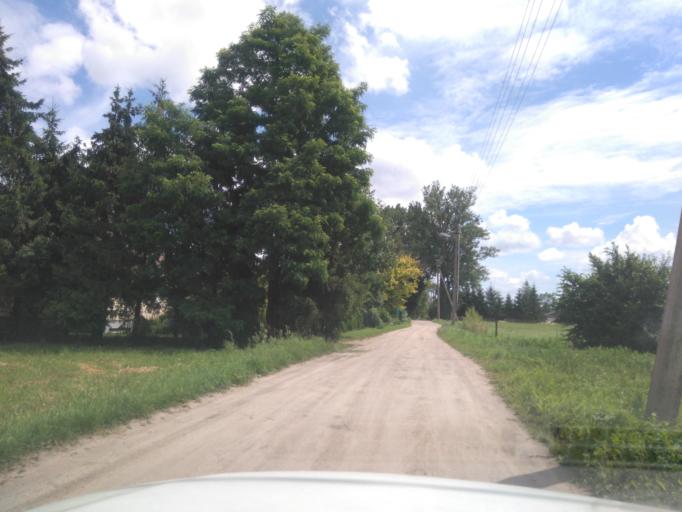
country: LT
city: Virbalis
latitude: 54.6301
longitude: 22.8250
